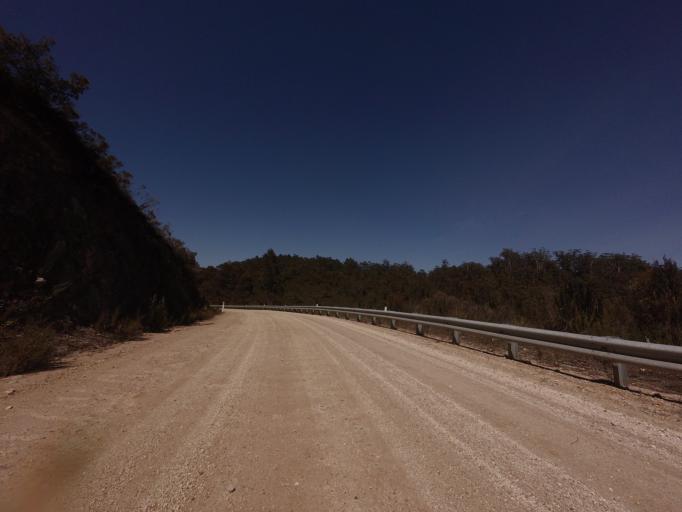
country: AU
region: Tasmania
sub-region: Huon Valley
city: Geeveston
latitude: -42.9812
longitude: 146.3640
